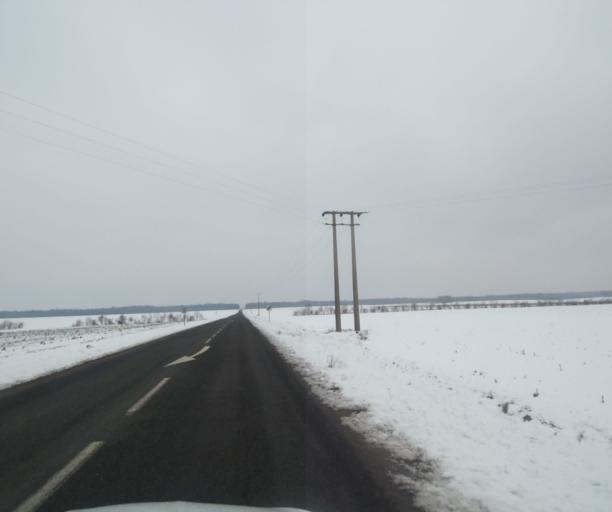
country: FR
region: Champagne-Ardenne
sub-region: Departement de la Haute-Marne
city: Villiers-en-Lieu
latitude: 48.5990
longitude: 4.8747
